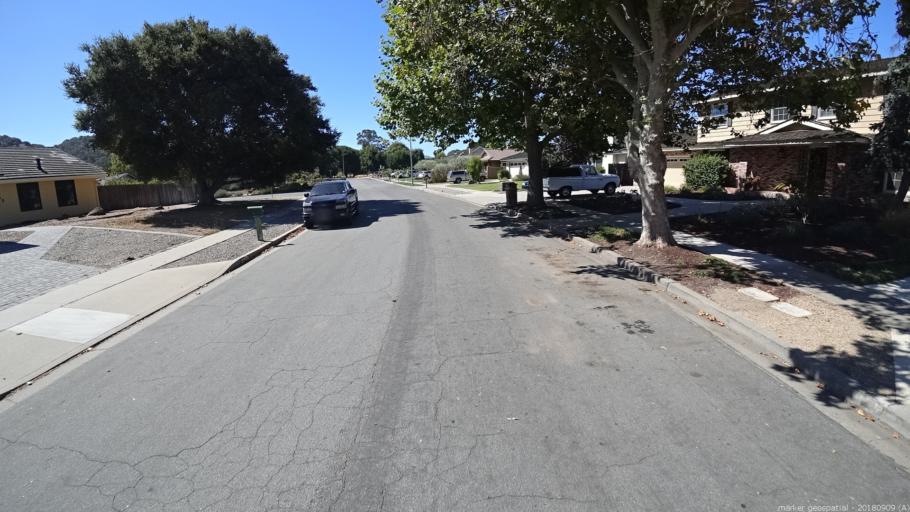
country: US
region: California
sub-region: Monterey County
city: Carmel Valley Village
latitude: 36.5918
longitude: -121.7115
